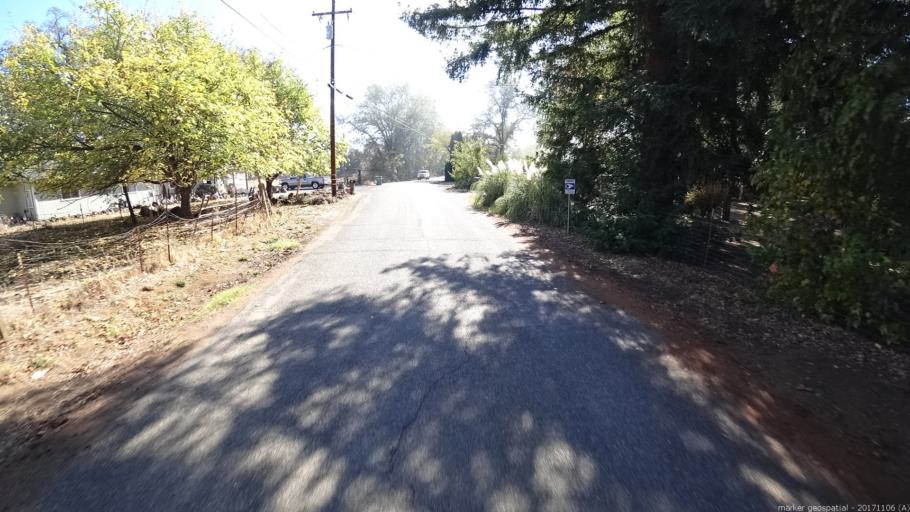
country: US
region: California
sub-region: Shasta County
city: Palo Cedro
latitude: 40.5819
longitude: -122.2958
